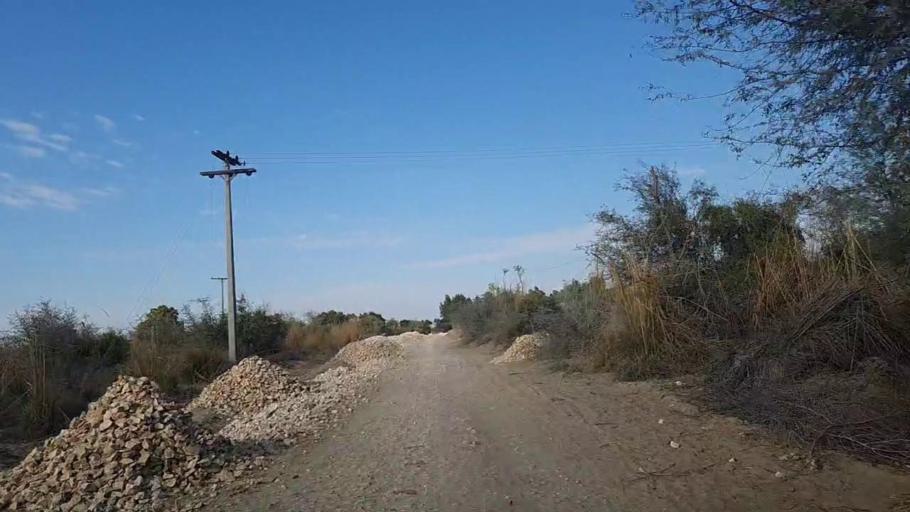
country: PK
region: Sindh
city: Jam Sahib
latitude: 26.3063
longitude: 68.8141
